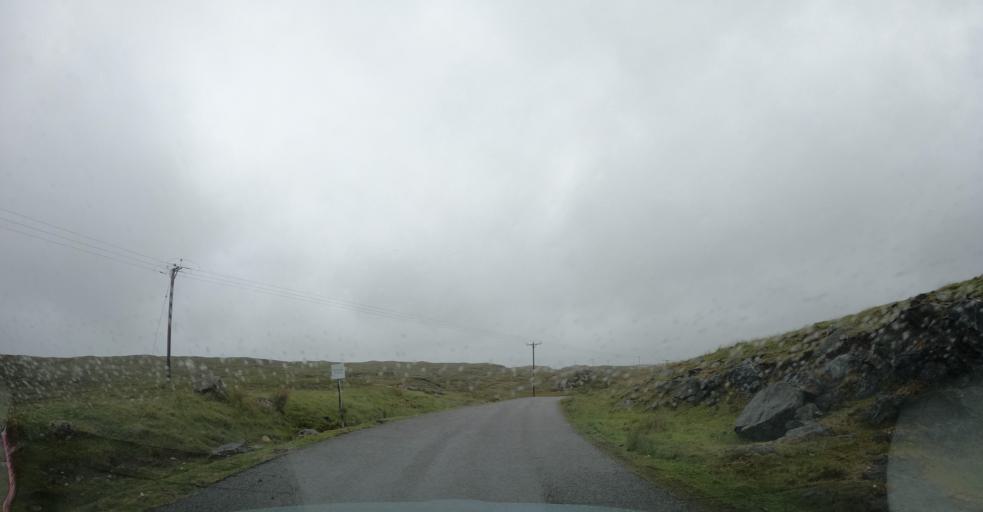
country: GB
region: Scotland
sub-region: Eilean Siar
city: Benbecula
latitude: 57.4953
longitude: -7.2363
